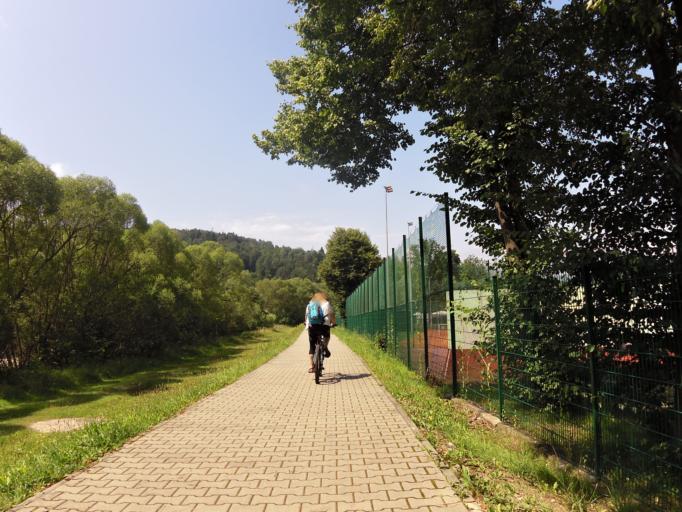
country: PL
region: Silesian Voivodeship
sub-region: Powiat zywiecki
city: Milowka
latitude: 49.5538
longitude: 19.0865
